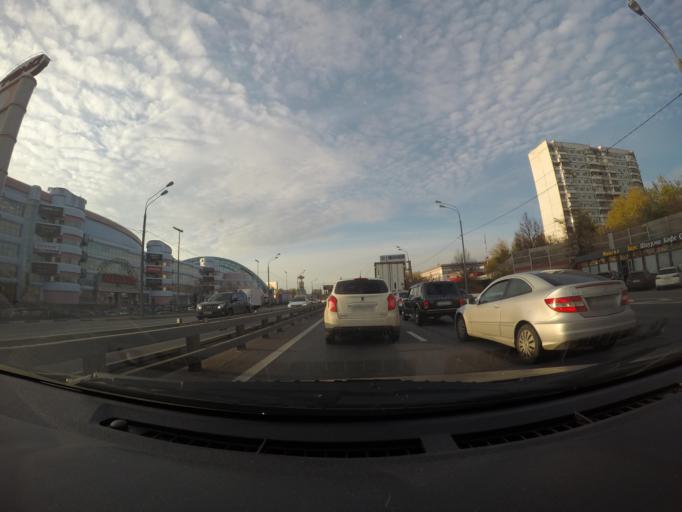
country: RU
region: Moscow
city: Khimki
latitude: 55.8865
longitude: 37.4390
